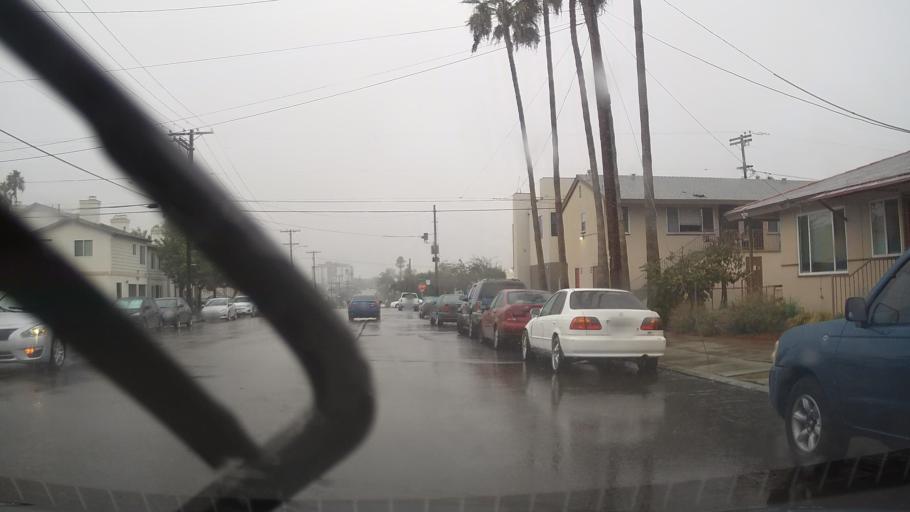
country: US
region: California
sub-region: San Diego County
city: San Diego
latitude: 32.7522
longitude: -117.1377
